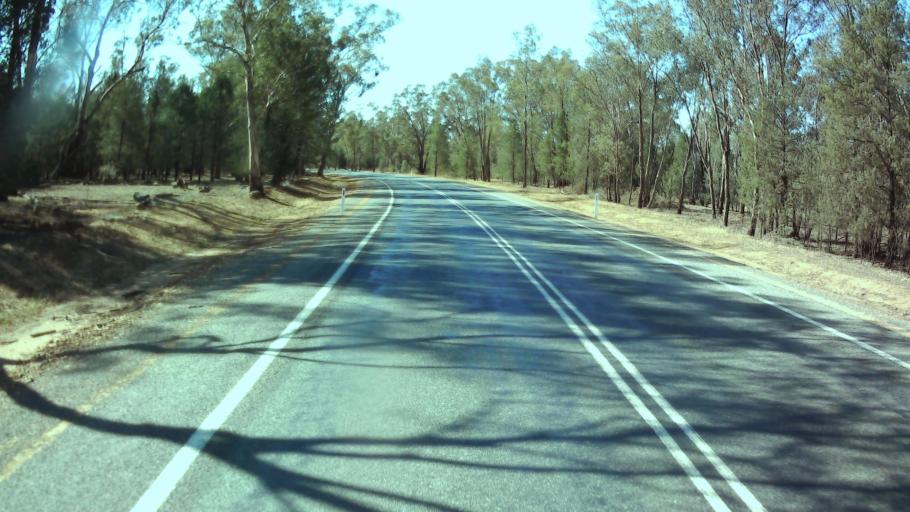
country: AU
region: New South Wales
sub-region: Weddin
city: Grenfell
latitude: -33.7288
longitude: 148.0885
